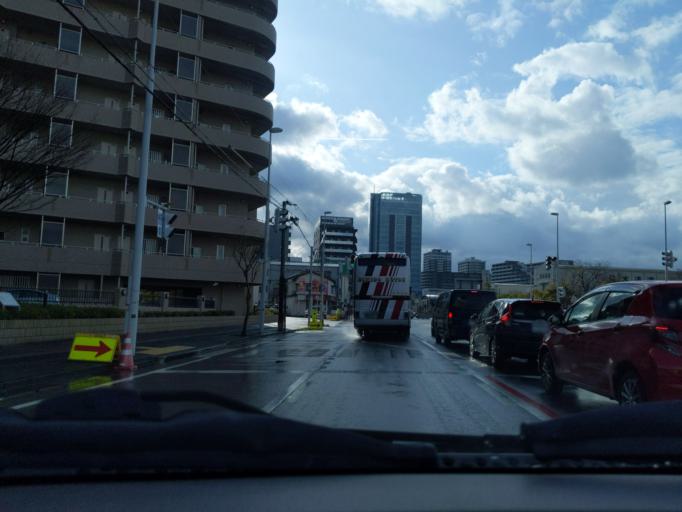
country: JP
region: Niigata
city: Niigata-shi
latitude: 37.9216
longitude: 139.0600
